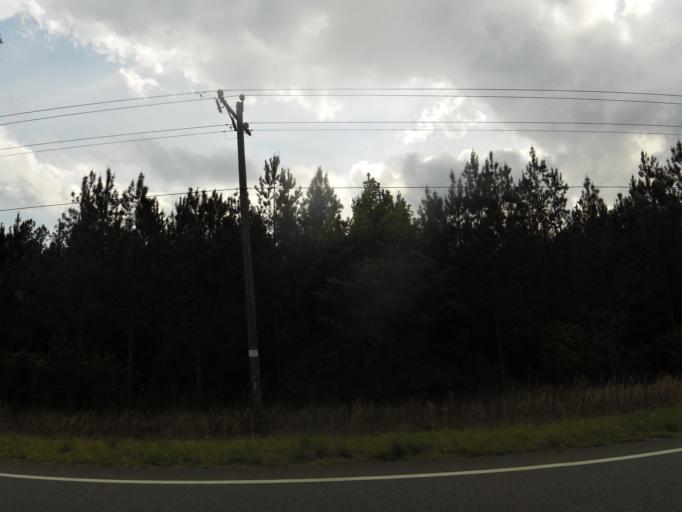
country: US
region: Florida
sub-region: Nassau County
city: Hilliard
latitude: 30.8195
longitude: -81.8531
